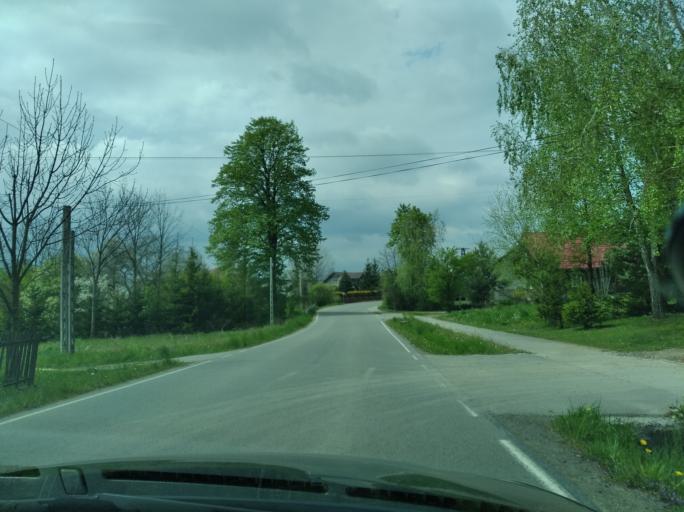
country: PL
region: Subcarpathian Voivodeship
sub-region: Powiat brzozowski
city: Haczow
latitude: 49.6451
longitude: 21.9337
